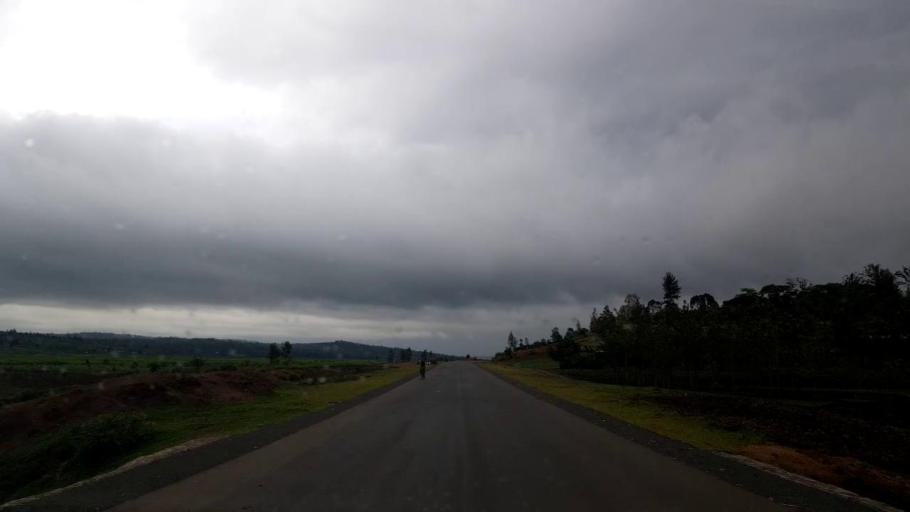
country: RW
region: Northern Province
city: Byumba
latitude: -1.4467
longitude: 30.2493
